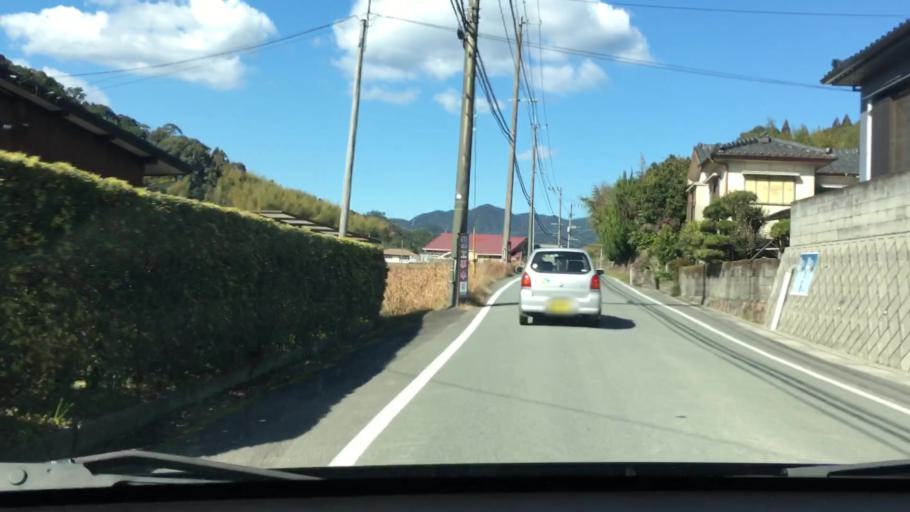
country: JP
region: Kagoshima
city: Ijuin
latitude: 31.6847
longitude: 130.4689
